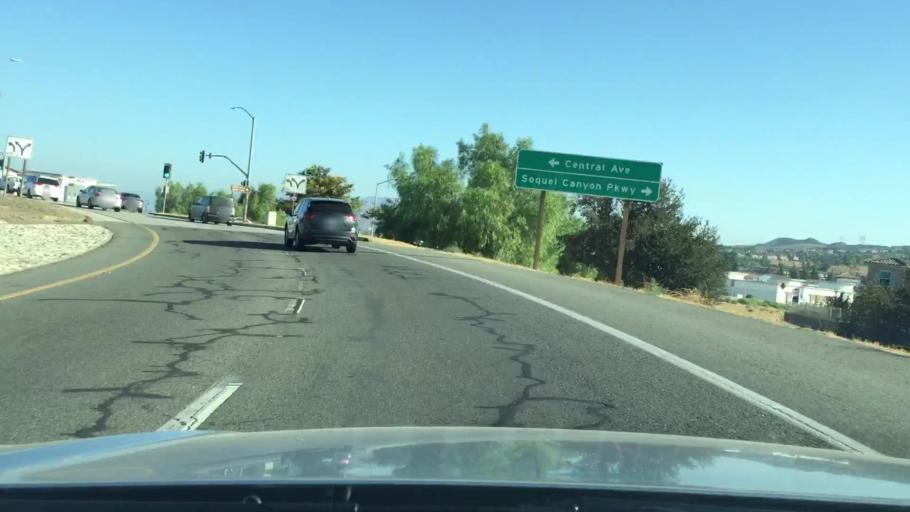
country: US
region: California
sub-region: San Bernardino County
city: Los Serranos
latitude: 33.9676
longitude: -117.6910
